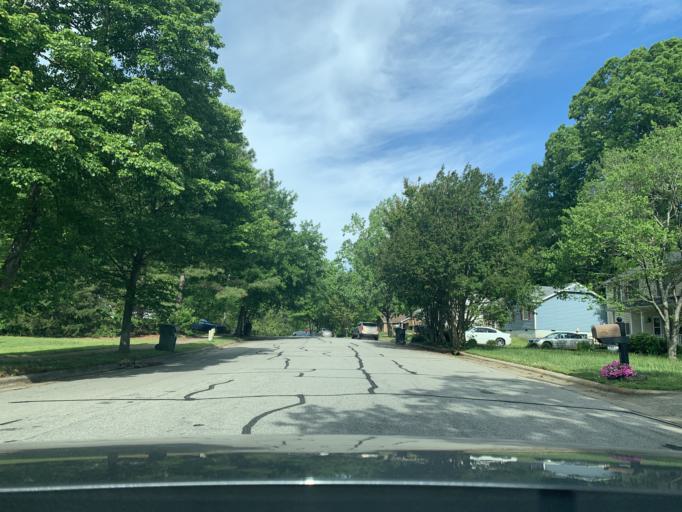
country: US
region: North Carolina
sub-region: Wake County
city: Garner
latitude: 35.7428
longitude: -78.6058
